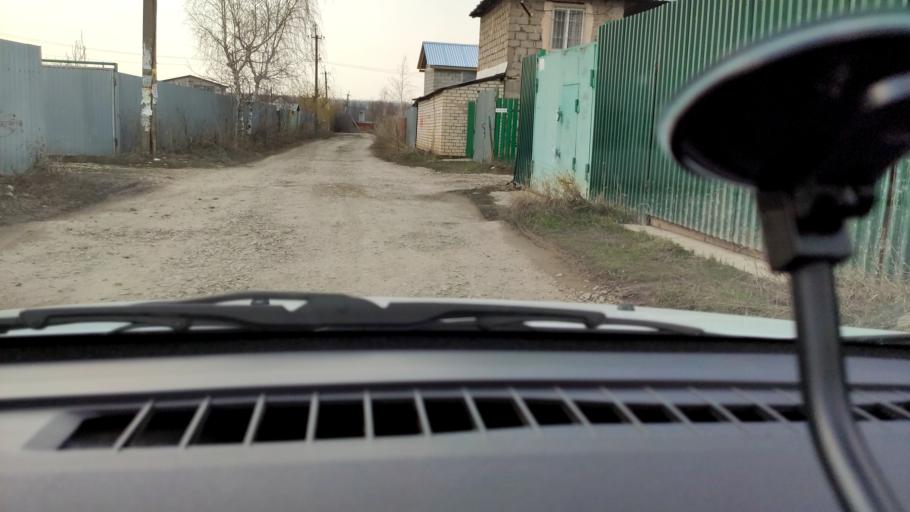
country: RU
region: Samara
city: Smyshlyayevka
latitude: 53.0913
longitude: 50.3949
